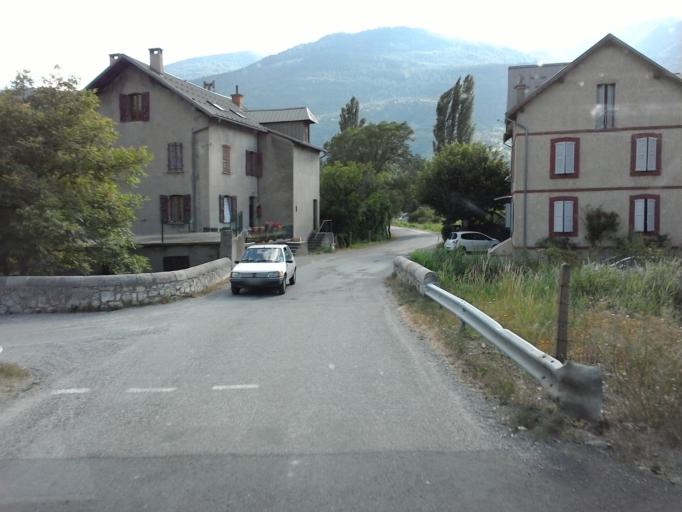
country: FR
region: Provence-Alpes-Cote d'Azur
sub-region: Departement des Hautes-Alpes
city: Guillestre
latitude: 44.7065
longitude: 6.6040
